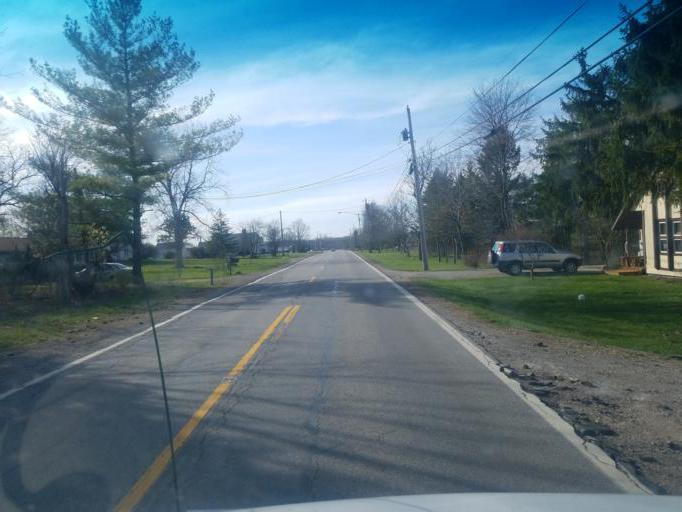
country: US
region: Ohio
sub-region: Union County
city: Marysville
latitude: 40.3361
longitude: -83.4687
